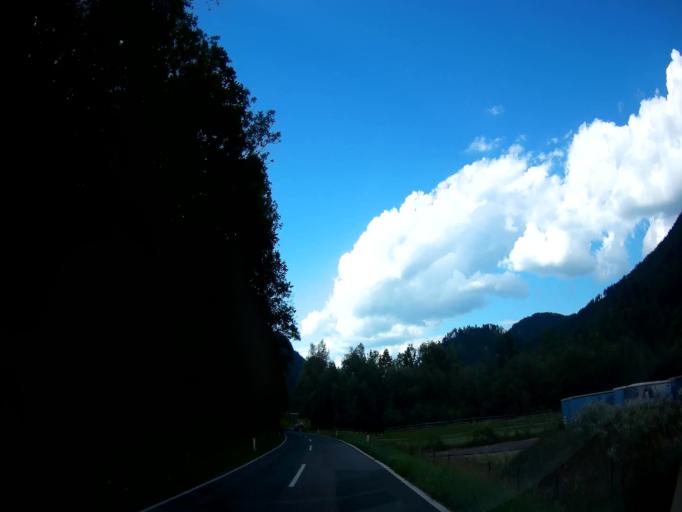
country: AT
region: Carinthia
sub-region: Politischer Bezirk Volkermarkt
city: Bad Eisenkappel
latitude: 46.5084
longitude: 14.5781
